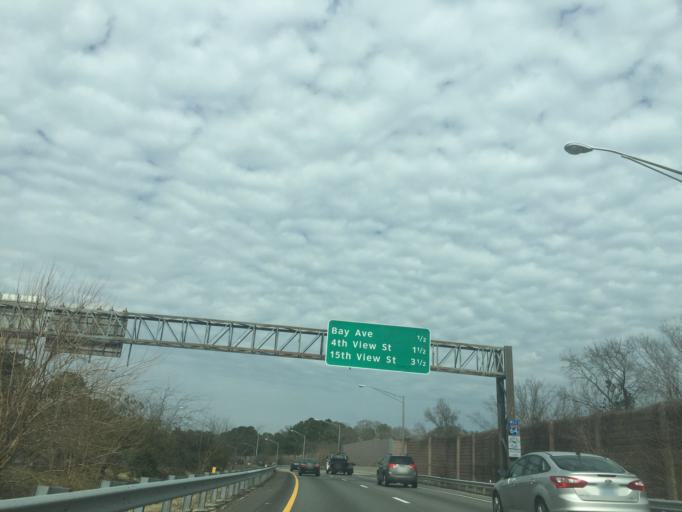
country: US
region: Virginia
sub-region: City of Norfolk
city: Norfolk
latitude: 36.9351
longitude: -76.2654
